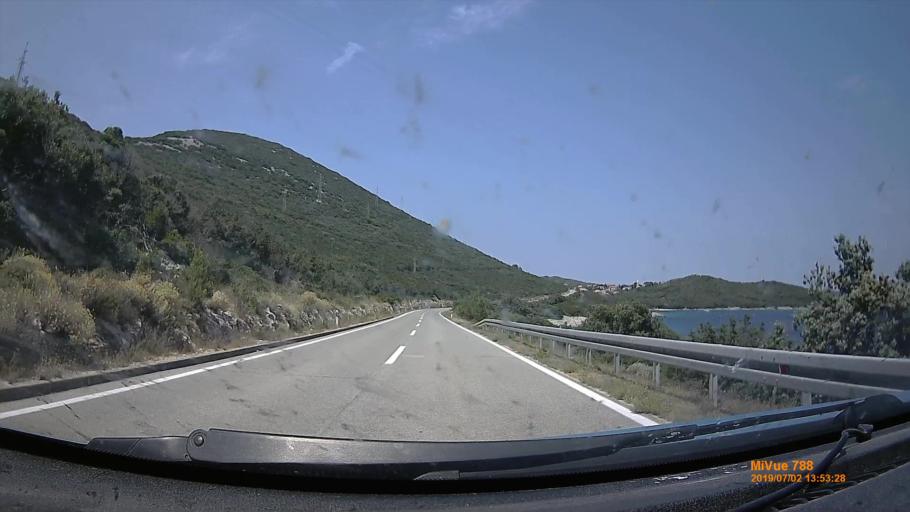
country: HR
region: Primorsko-Goranska
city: Mali Losinj
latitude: 44.6268
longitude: 14.3929
